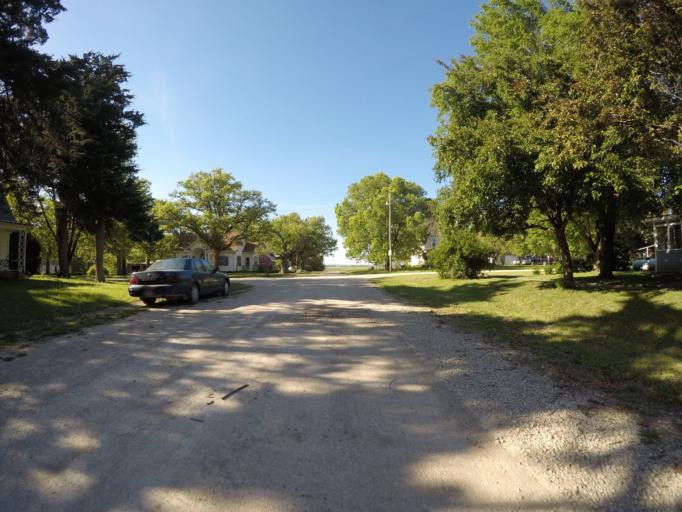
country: US
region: Kansas
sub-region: Clay County
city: Clay Center
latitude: 39.4330
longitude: -96.9971
